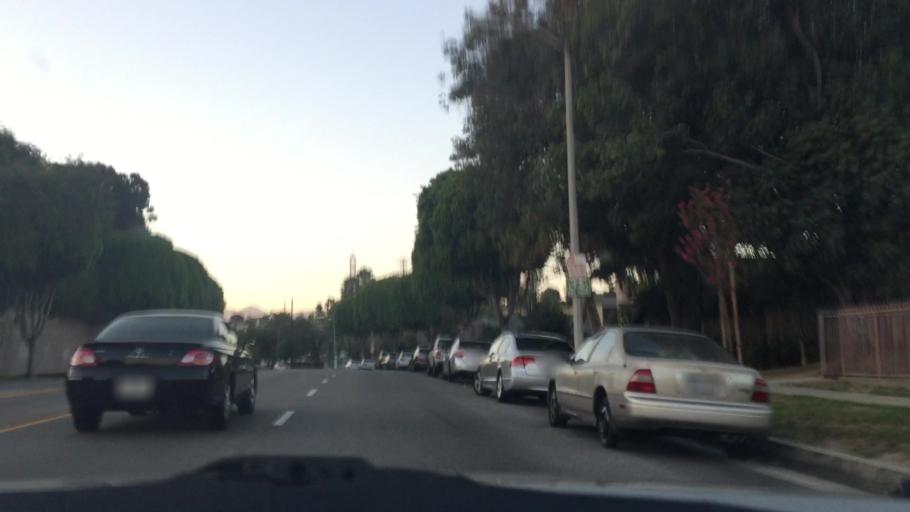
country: US
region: California
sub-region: Los Angeles County
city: Monterey Park
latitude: 34.0429
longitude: -118.1286
